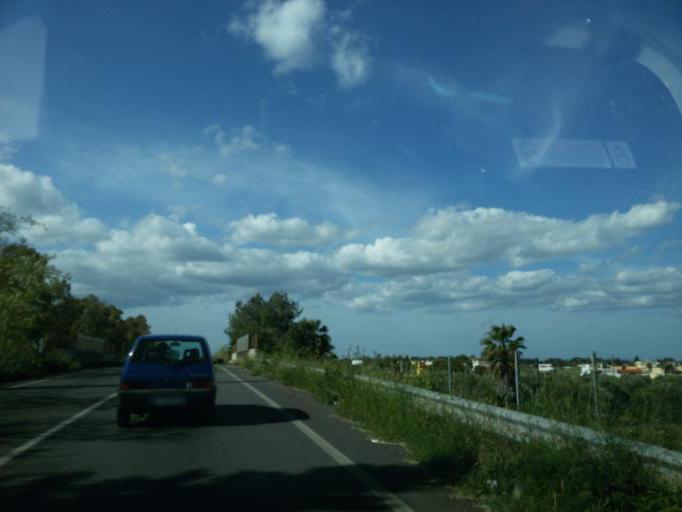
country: IT
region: Apulia
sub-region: Provincia di Brindisi
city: Mesagne
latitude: 40.5597
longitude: 17.7879
